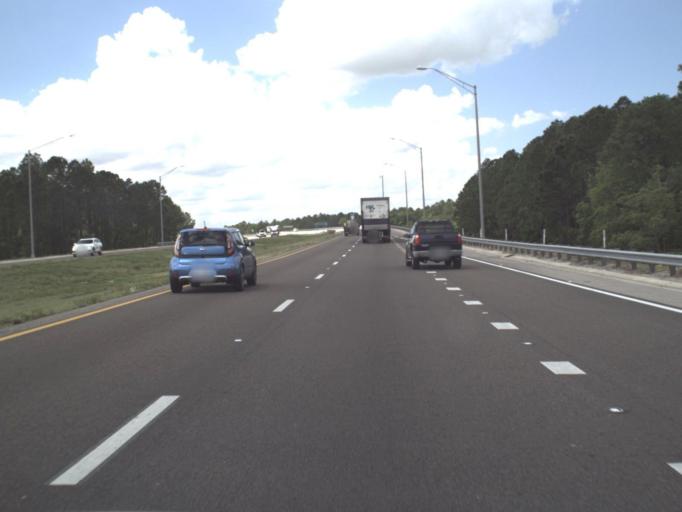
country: US
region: Florida
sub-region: Orange County
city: Paradise Heights
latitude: 28.5992
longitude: -81.5502
